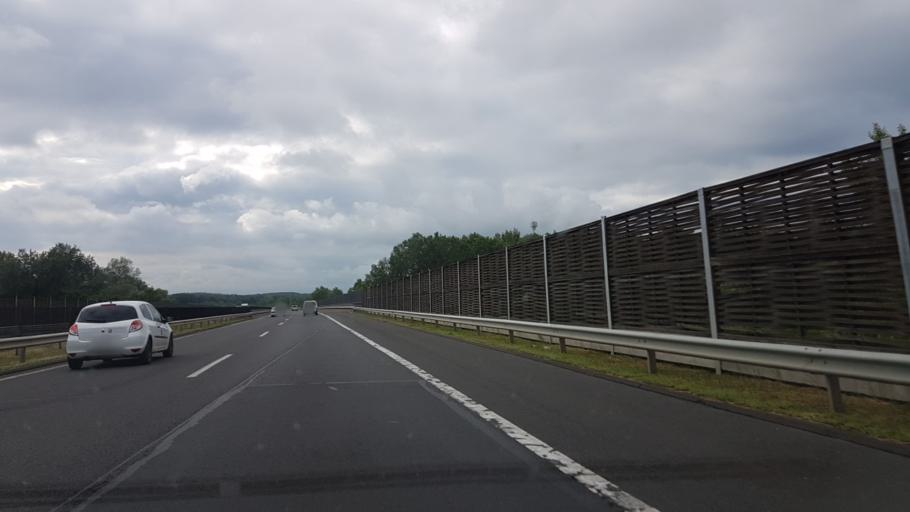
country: HU
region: Hajdu-Bihar
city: Polgar
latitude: 47.8577
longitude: 21.0513
